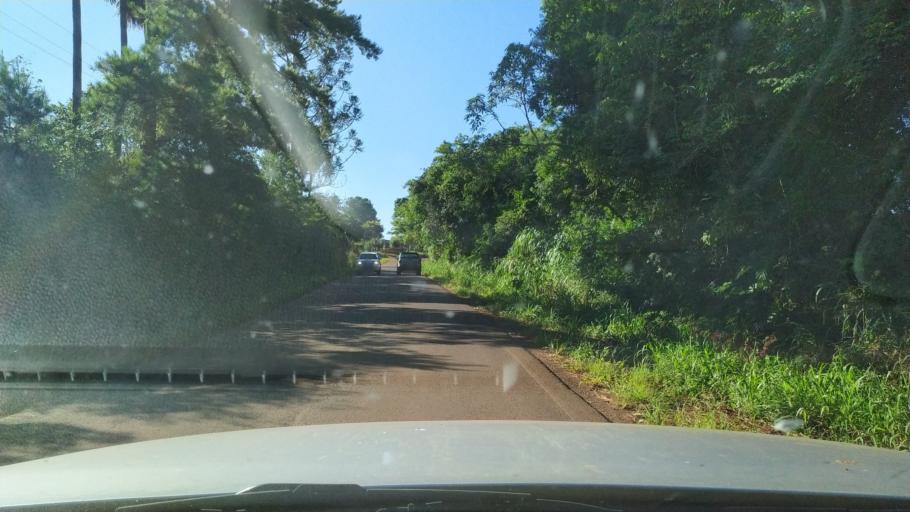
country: AR
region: Misiones
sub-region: Departamento de Montecarlo
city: Montecarlo
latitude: -26.5990
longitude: -54.7032
